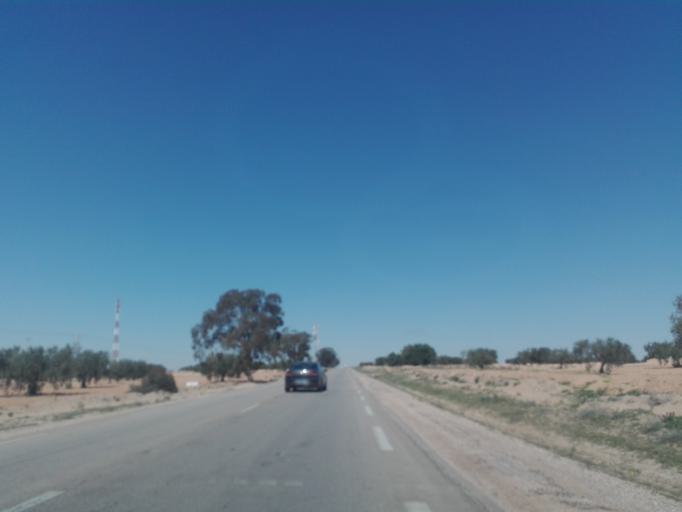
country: TN
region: Safaqis
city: Bi'r `Ali Bin Khalifah
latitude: 34.7543
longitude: 10.3349
